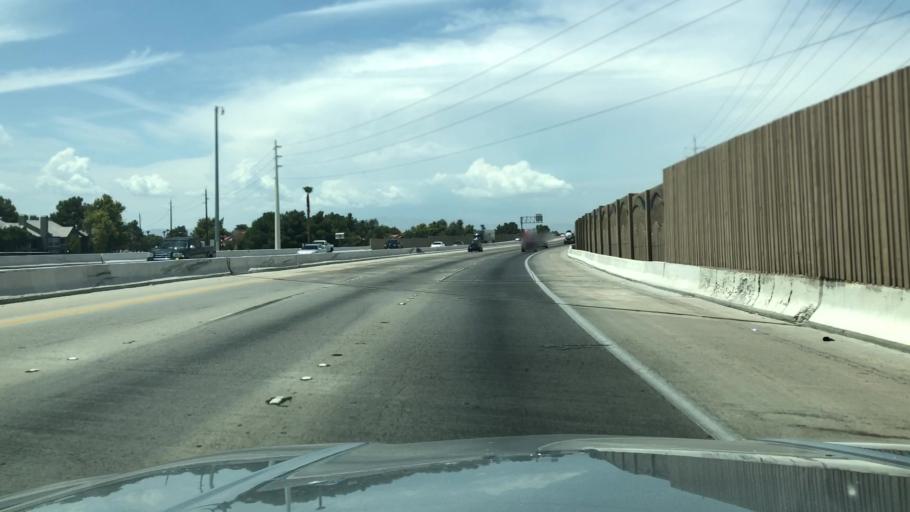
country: US
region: Nevada
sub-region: Clark County
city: Whitney
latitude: 36.0891
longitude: -115.0677
